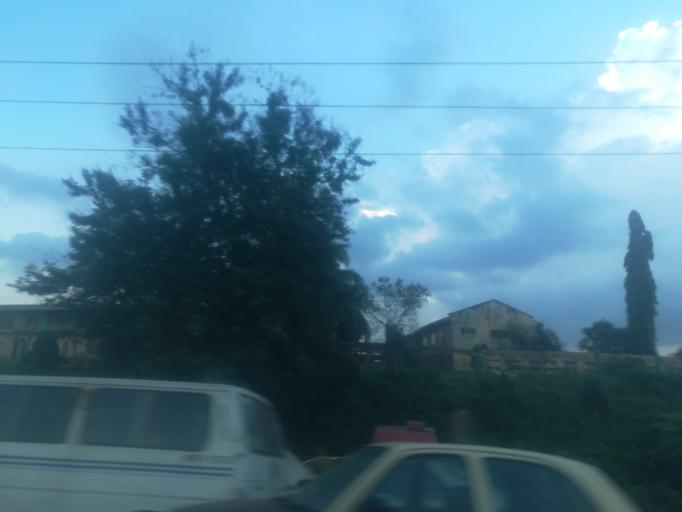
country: NG
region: Oyo
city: Ibadan
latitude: 7.4402
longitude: 3.9244
